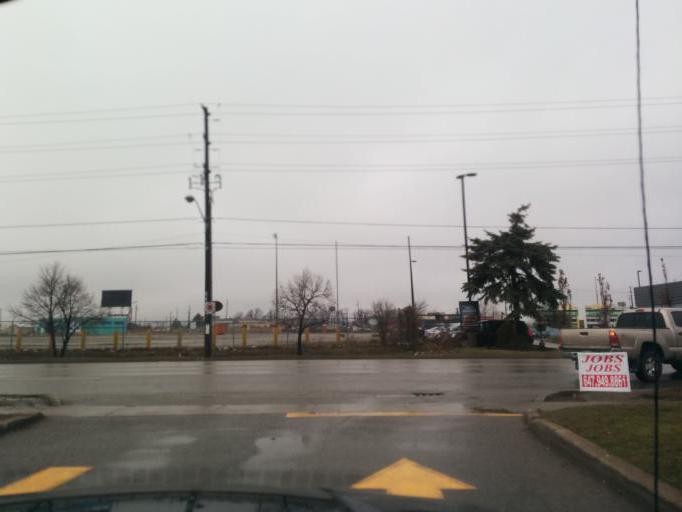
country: CA
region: Ontario
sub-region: Halton
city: Milton
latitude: 43.5232
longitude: -79.9005
